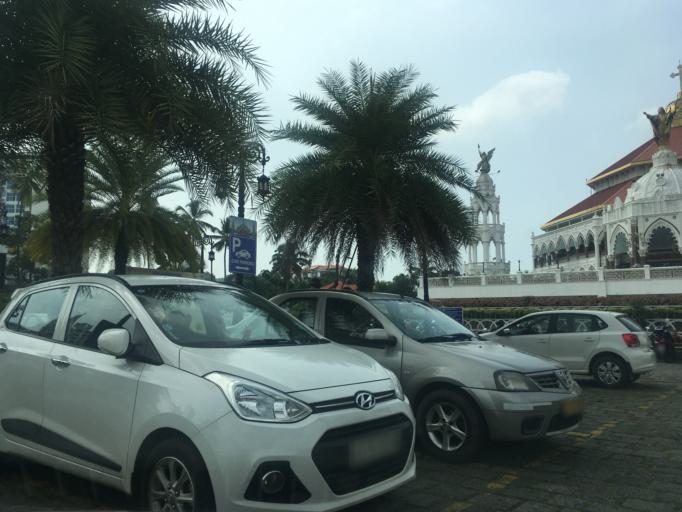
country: IN
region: Kerala
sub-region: Ernakulam
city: Elur
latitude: 10.0219
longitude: 76.3057
